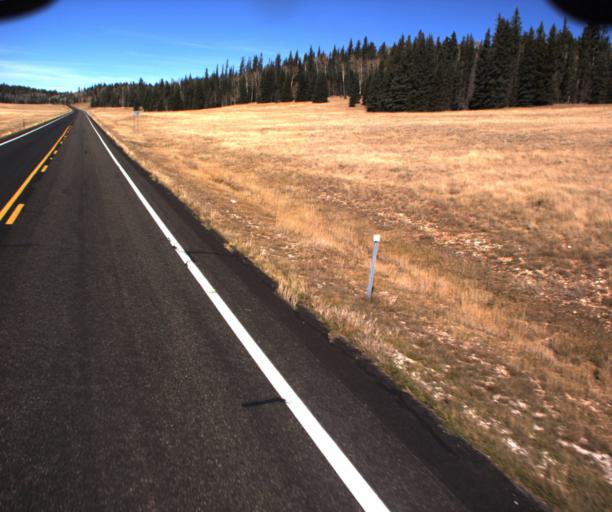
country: US
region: Arizona
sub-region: Coconino County
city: Grand Canyon
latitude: 36.4265
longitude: -112.1315
